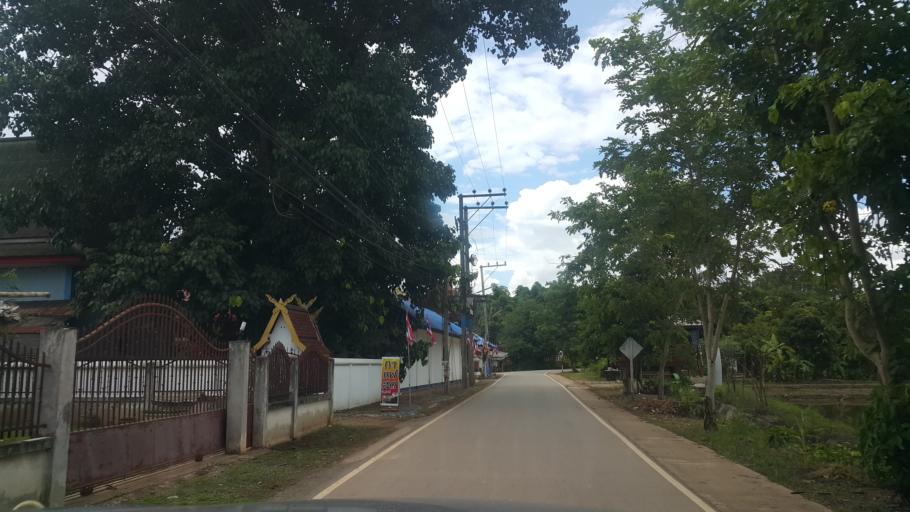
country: TH
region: Chiang Mai
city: Mae Taeng
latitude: 19.1908
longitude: 98.9958
